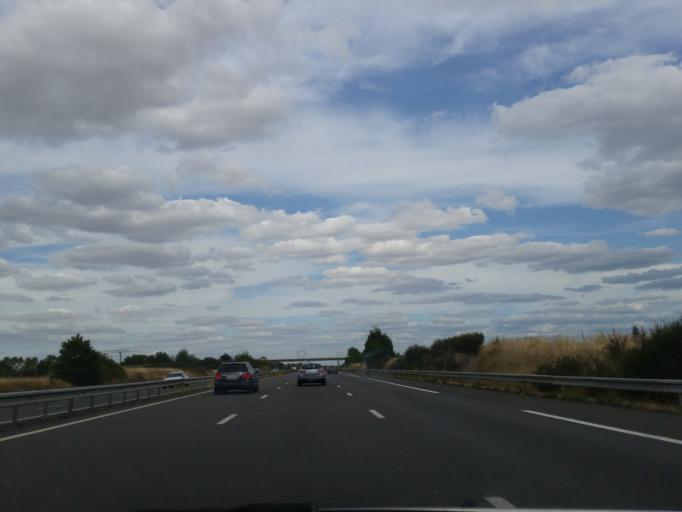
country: FR
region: Centre
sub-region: Departement du Loir-et-Cher
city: Herbault
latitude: 47.6085
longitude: 1.1290
